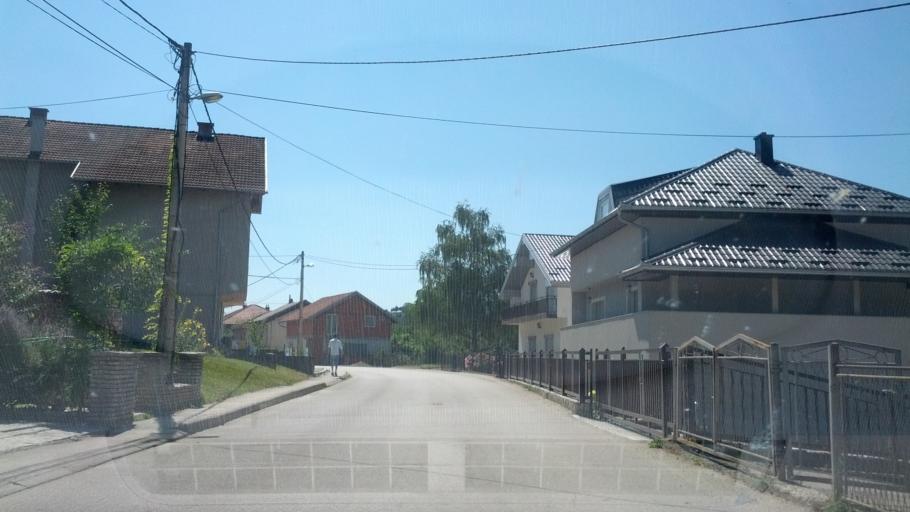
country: BA
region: Federation of Bosnia and Herzegovina
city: Bosanska Krupa
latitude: 44.8876
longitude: 16.1396
